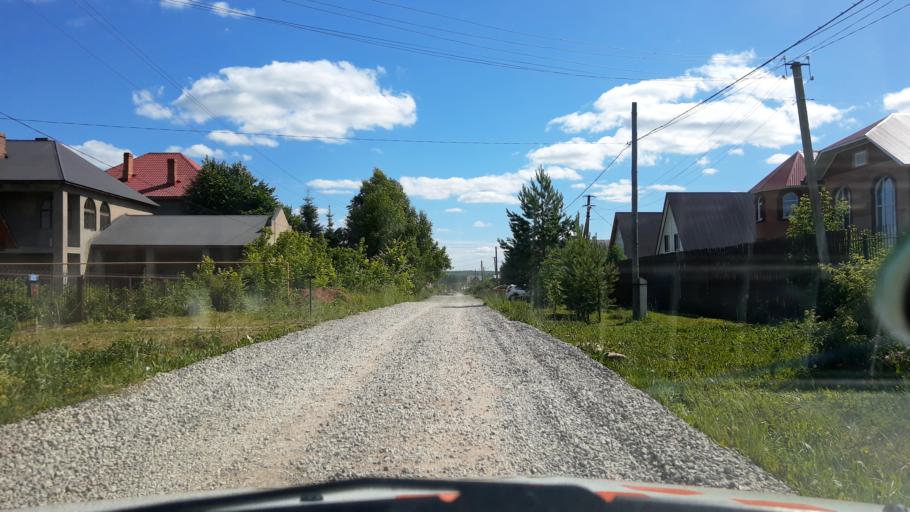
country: RU
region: Bashkortostan
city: Iglino
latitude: 54.8489
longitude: 56.4231
